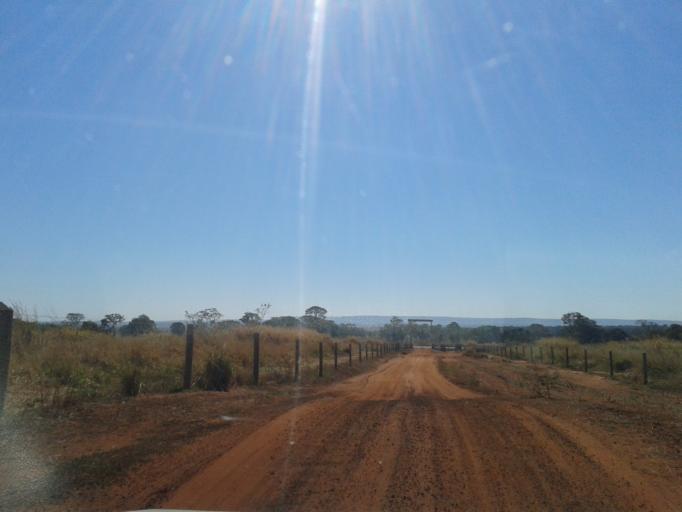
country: BR
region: Minas Gerais
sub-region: Santa Vitoria
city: Santa Vitoria
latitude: -19.1422
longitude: -50.2019
